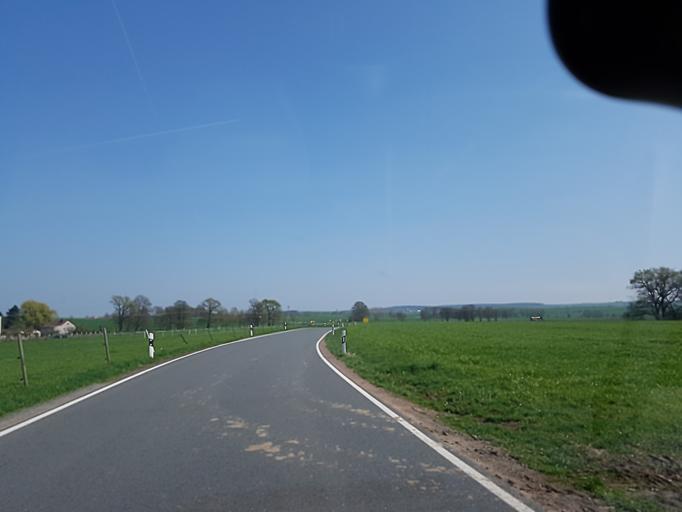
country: DE
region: Saxony
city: Cavertitz
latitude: 51.3897
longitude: 13.0921
